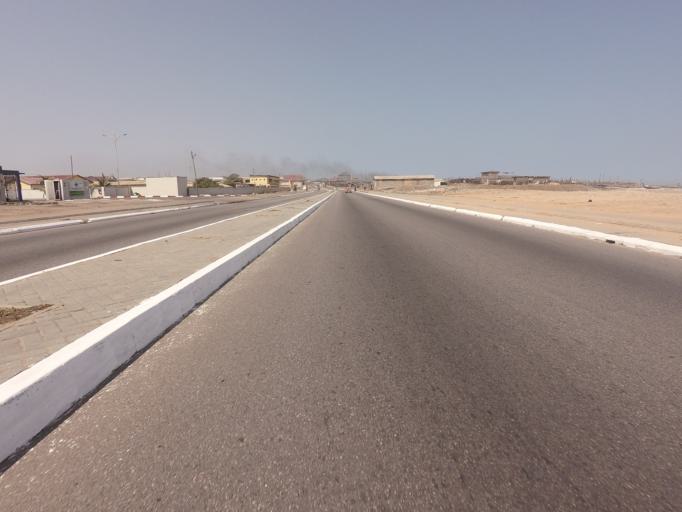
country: GH
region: Greater Accra
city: Accra
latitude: 5.5316
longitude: -0.2184
